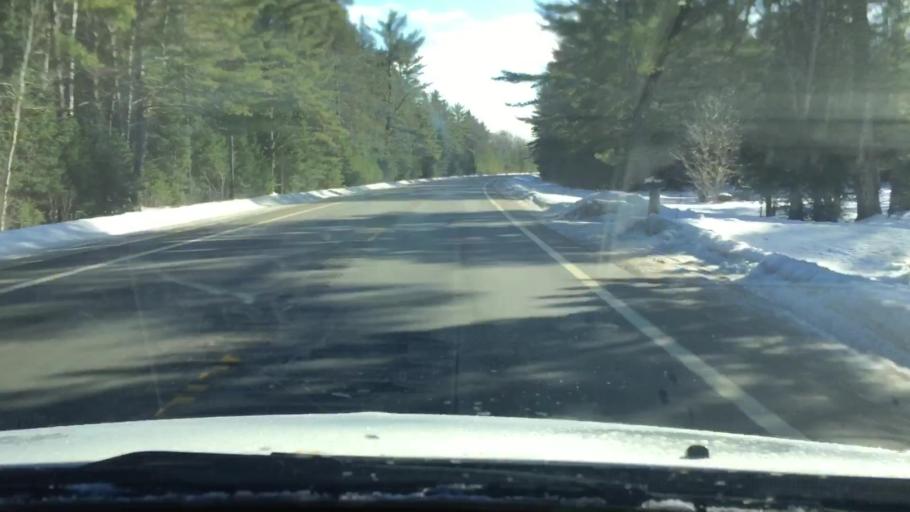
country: US
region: Michigan
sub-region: Charlevoix County
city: East Jordan
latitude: 45.0538
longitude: -85.0719
